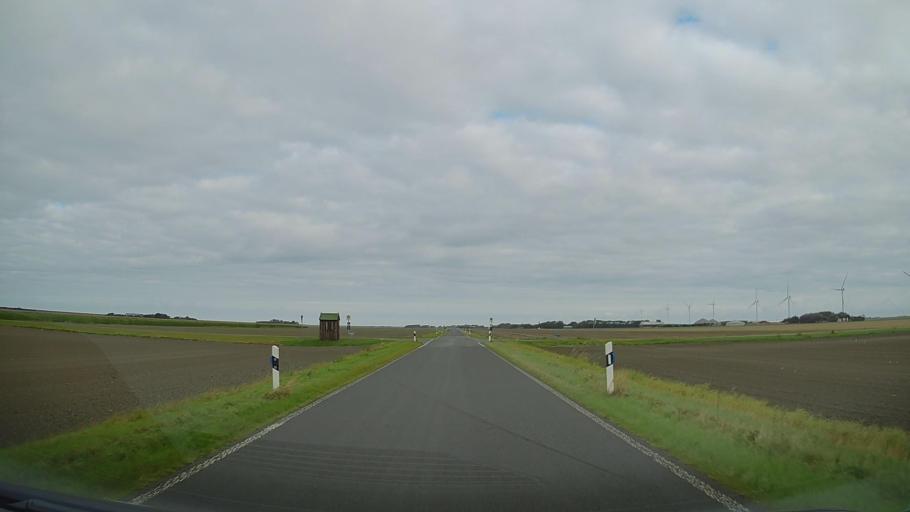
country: DE
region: Schleswig-Holstein
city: Friedrich-Wilhelm-Lubke-Koog
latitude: 54.8494
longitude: 8.6229
